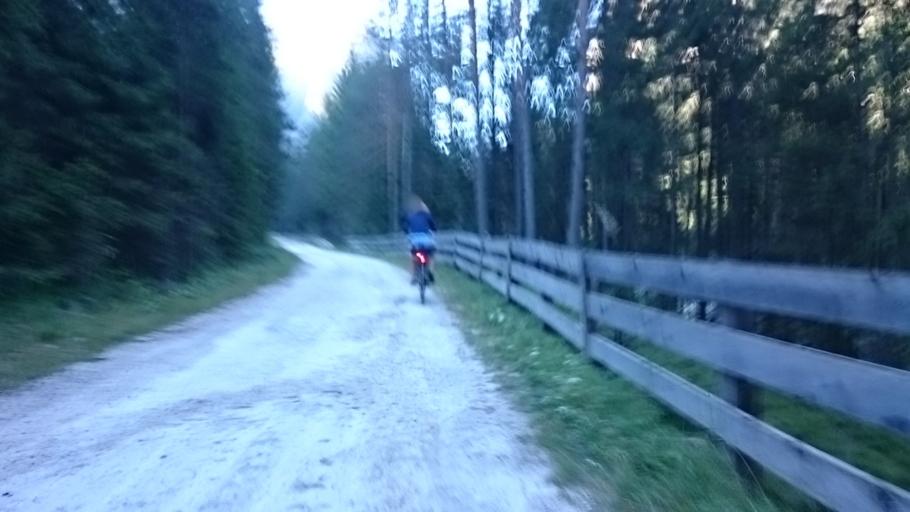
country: IT
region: Trentino-Alto Adige
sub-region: Bolzano
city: Dobbiaco
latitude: 46.6943
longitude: 12.2225
